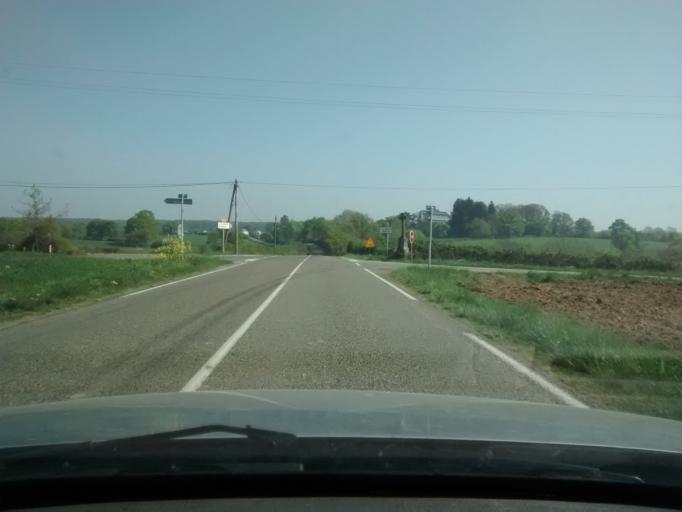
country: FR
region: Pays de la Loire
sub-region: Departement de la Mayenne
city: Soulge-sur-Ouette
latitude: 48.0918
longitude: -0.5285
